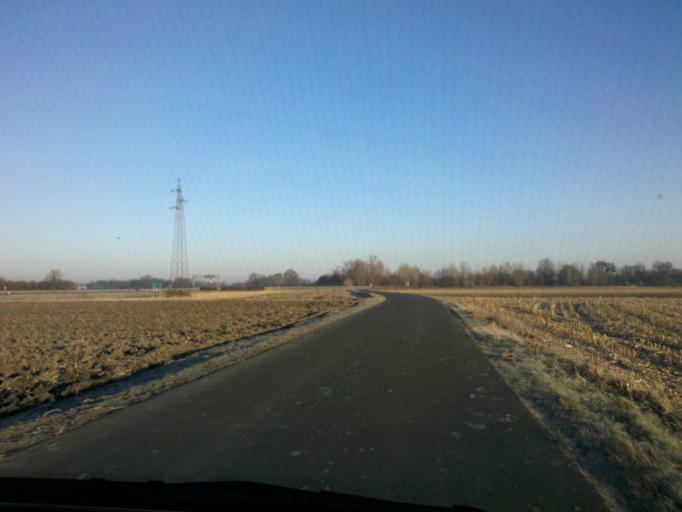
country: HR
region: Medimurska
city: Mala Subotica
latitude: 46.3518
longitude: 16.5371
